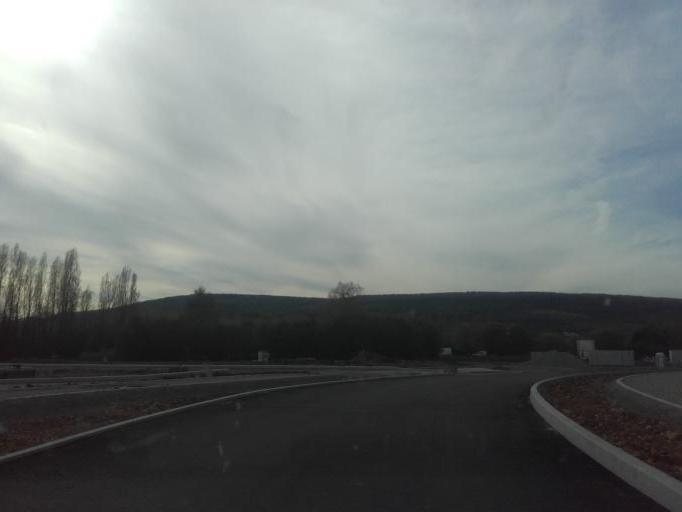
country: FR
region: Bourgogne
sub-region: Departement de la Cote-d'Or
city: Corpeau
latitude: 46.9230
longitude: 4.7398
